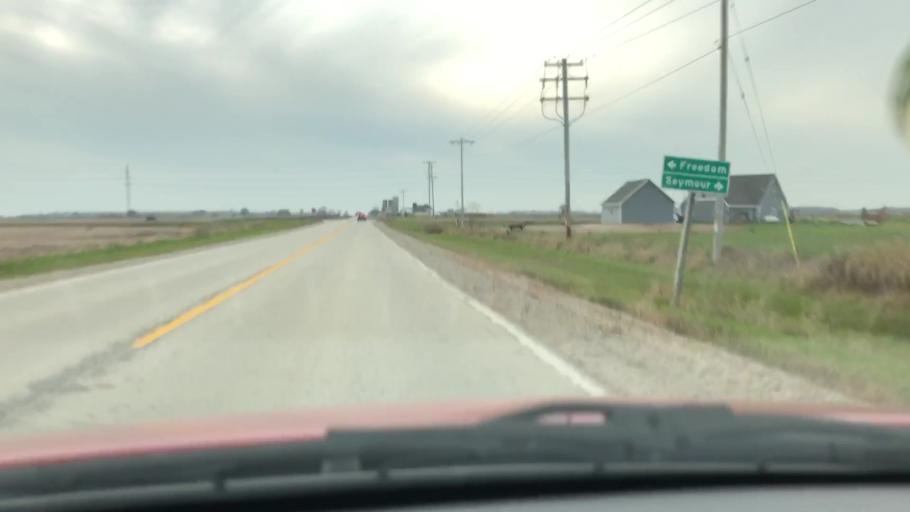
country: US
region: Wisconsin
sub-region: Outagamie County
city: Seymour
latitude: 44.4439
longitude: -88.2890
